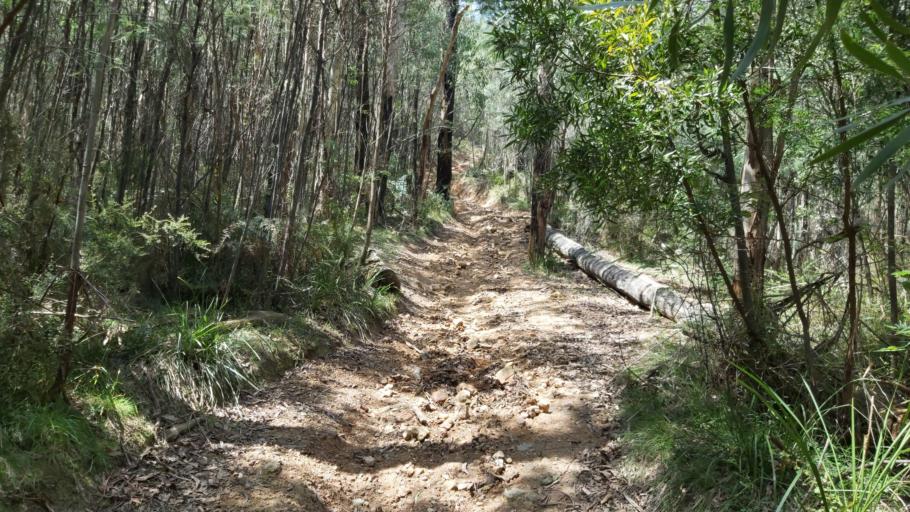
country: AU
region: Victoria
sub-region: Murrindindi
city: Kinglake West
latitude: -37.4296
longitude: 145.2695
